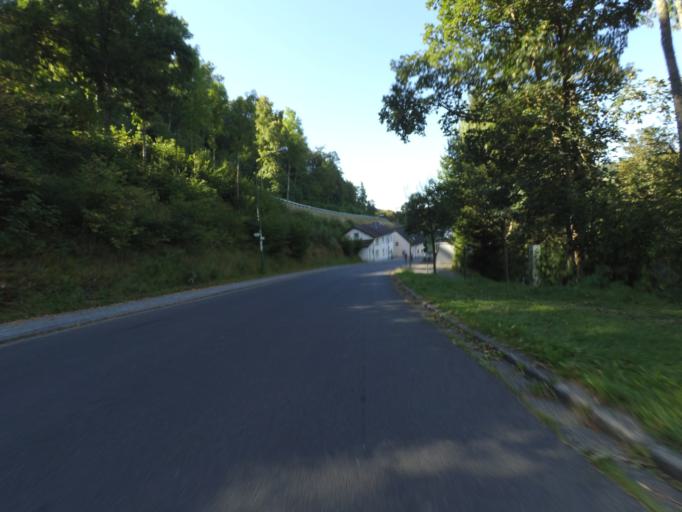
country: DE
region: Rheinland-Pfalz
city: Daun
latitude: 50.1812
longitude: 6.8337
